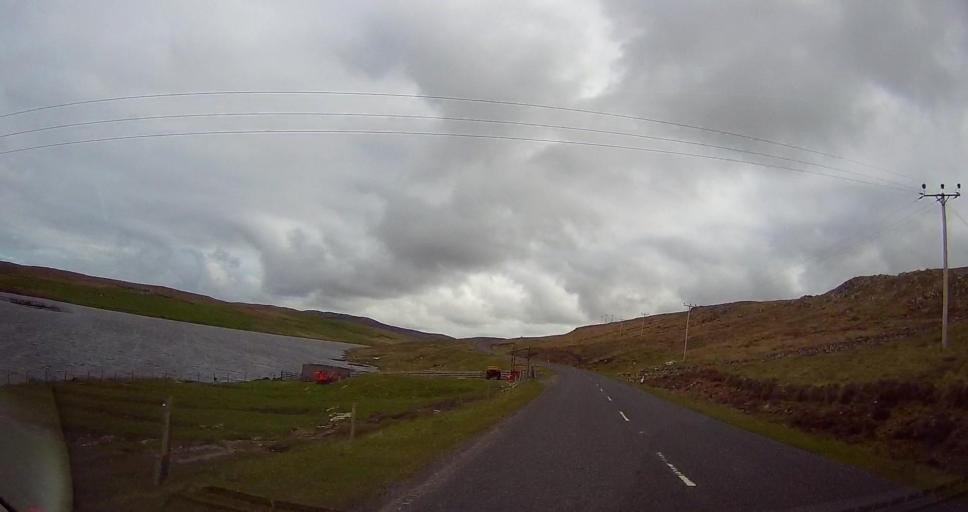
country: GB
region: Scotland
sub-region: Shetland Islands
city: Shetland
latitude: 60.6899
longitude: -0.9599
